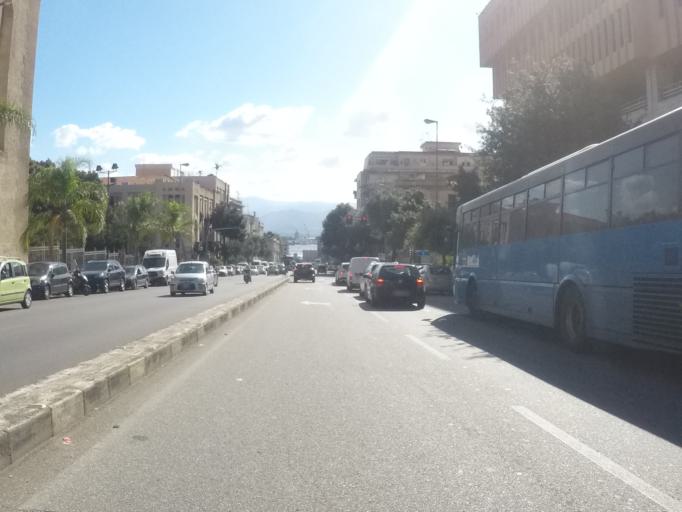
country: IT
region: Sicily
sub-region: Messina
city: Messina
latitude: 38.1980
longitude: 15.5536
